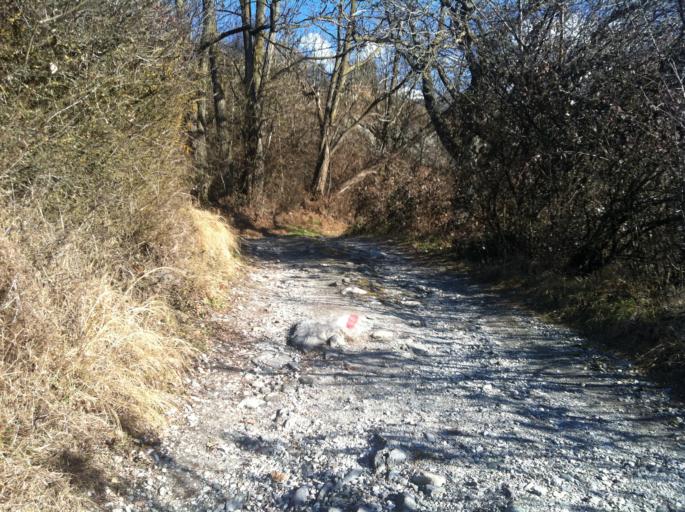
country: IT
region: Trentino-Alto Adige
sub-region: Bolzano
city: Leone-Santa Elisabetta
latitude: 46.7322
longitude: 11.6645
